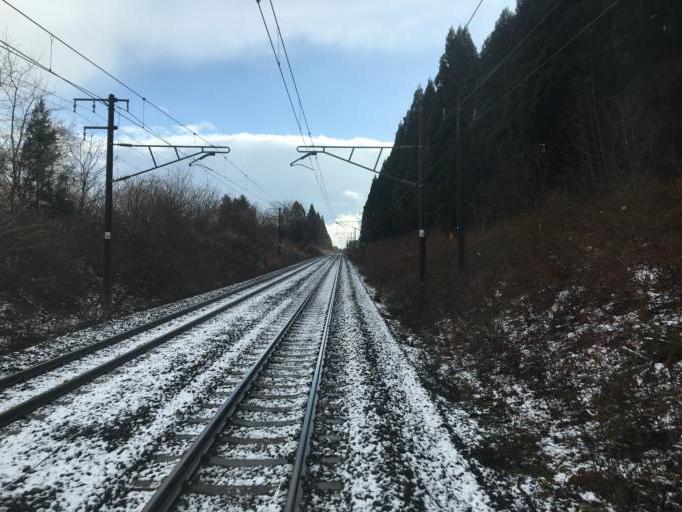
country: JP
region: Aomori
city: Aomori Shi
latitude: 40.9109
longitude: 141.0485
